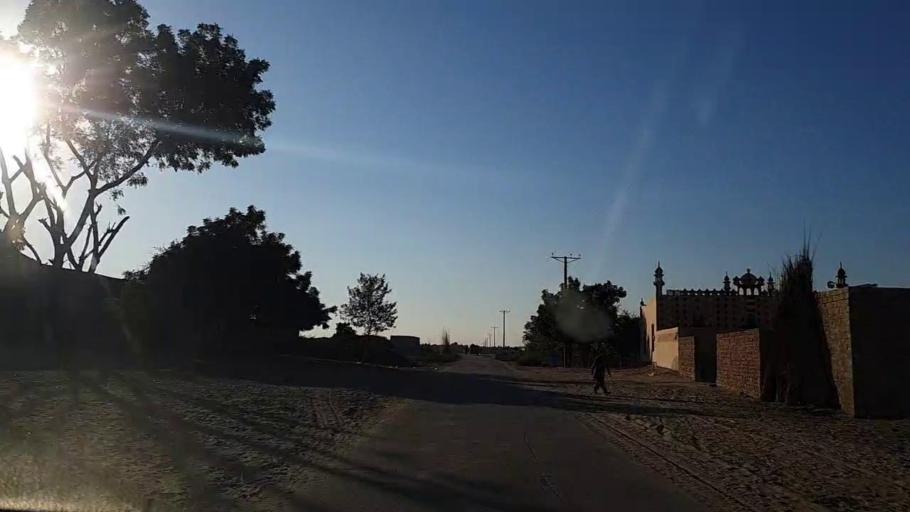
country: PK
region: Sindh
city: Sanghar
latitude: 26.2790
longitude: 68.9175
